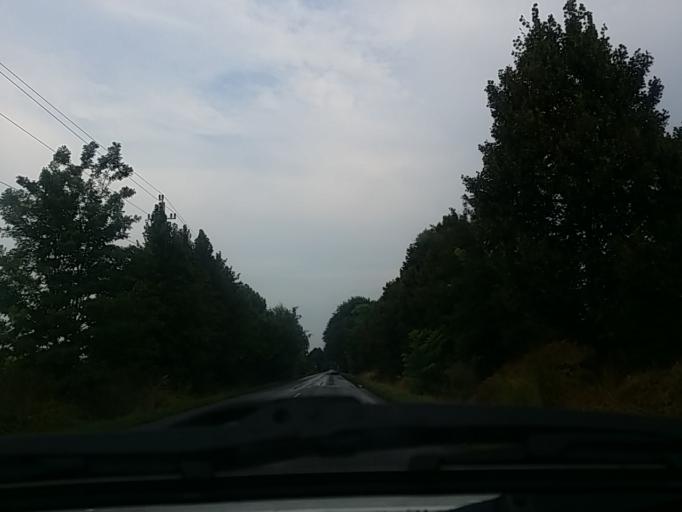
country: HU
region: Pest
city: Paty
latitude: 47.5147
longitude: 18.8081
